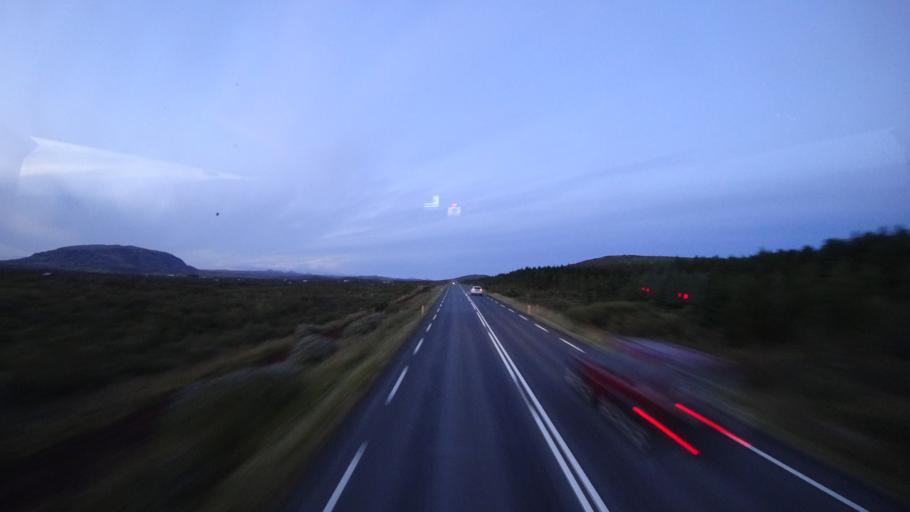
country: IS
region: South
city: Selfoss
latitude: 64.0333
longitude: -20.9017
